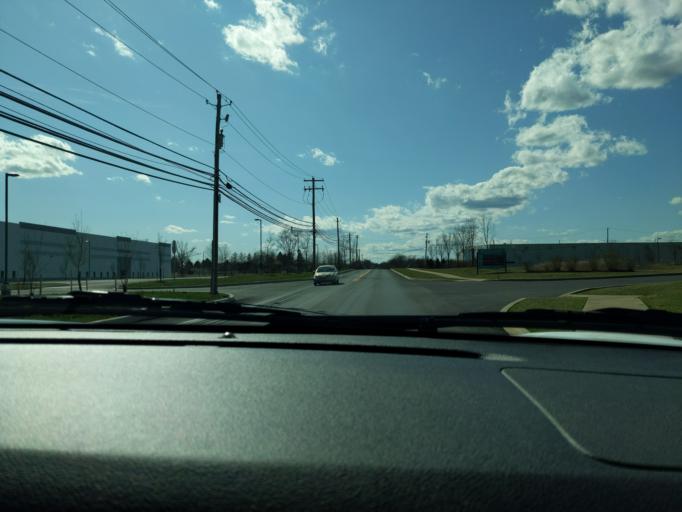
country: US
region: Pennsylvania
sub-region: Bucks County
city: Quakertown
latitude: 40.4399
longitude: -75.3727
